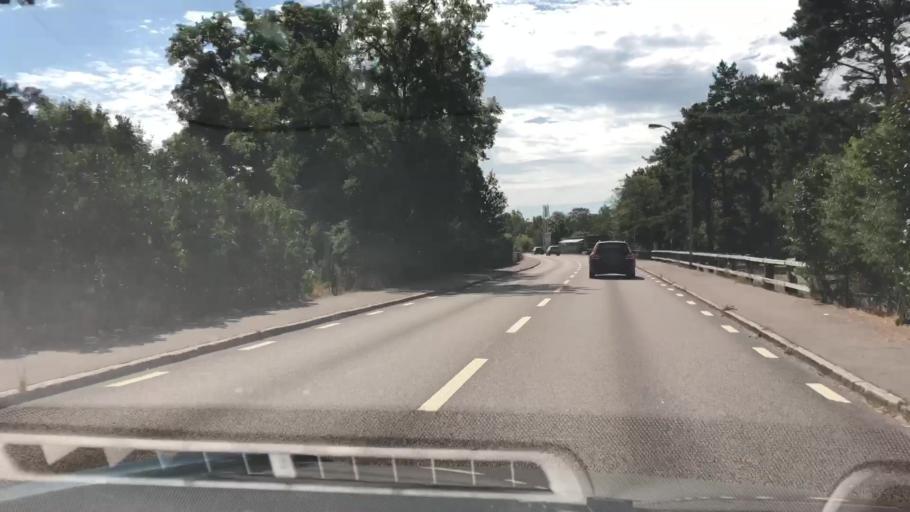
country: SE
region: Kalmar
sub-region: Torsas Kommun
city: Torsas
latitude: 56.3897
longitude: 16.0668
